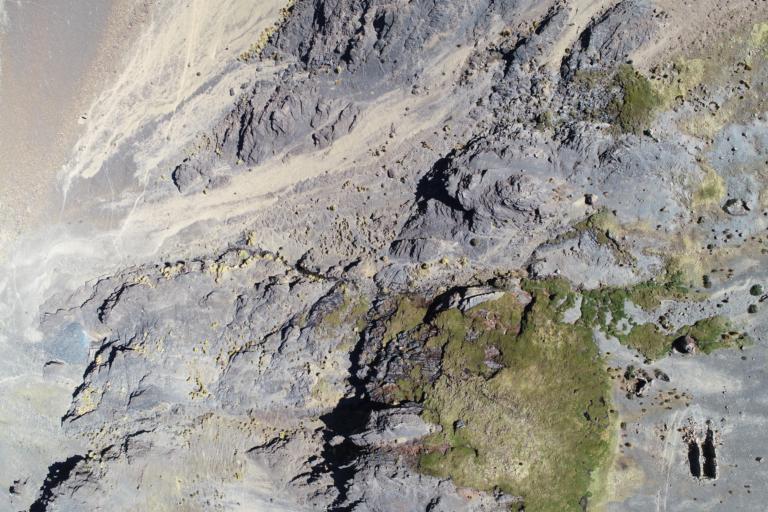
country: BO
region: La Paz
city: La Paz
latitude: -16.6183
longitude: -67.8237
